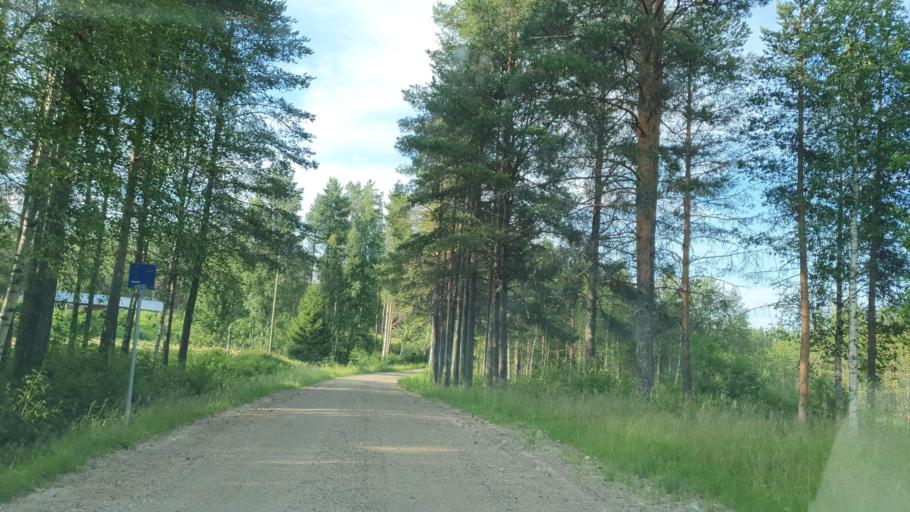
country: FI
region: Kainuu
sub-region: Kehys-Kainuu
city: Kuhmo
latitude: 64.3114
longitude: 29.5625
